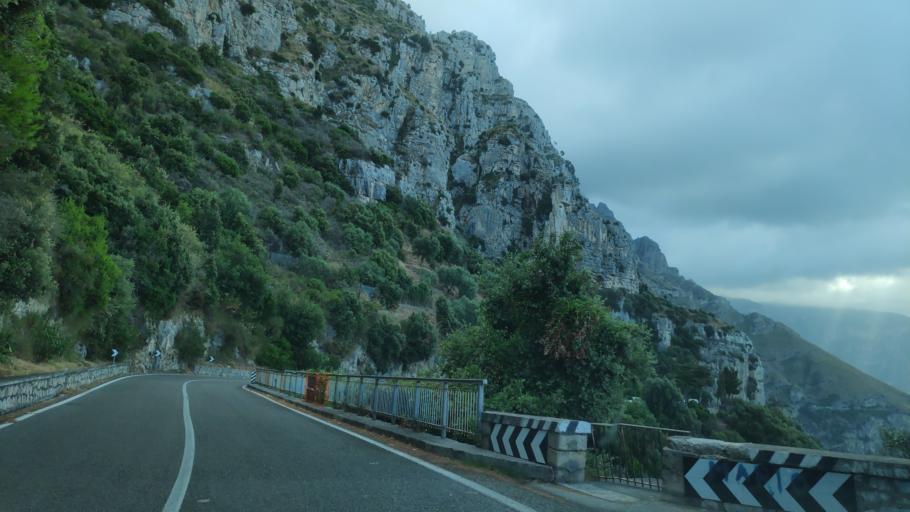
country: IT
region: Campania
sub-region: Provincia di Napoli
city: Arola-Preazzano
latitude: 40.6168
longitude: 14.4387
